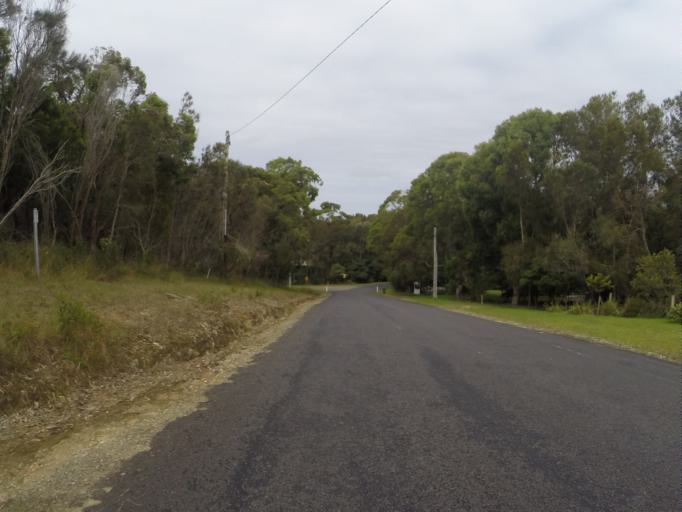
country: AU
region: New South Wales
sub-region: Eurobodalla
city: Broulee
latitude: -35.8297
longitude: 150.2217
